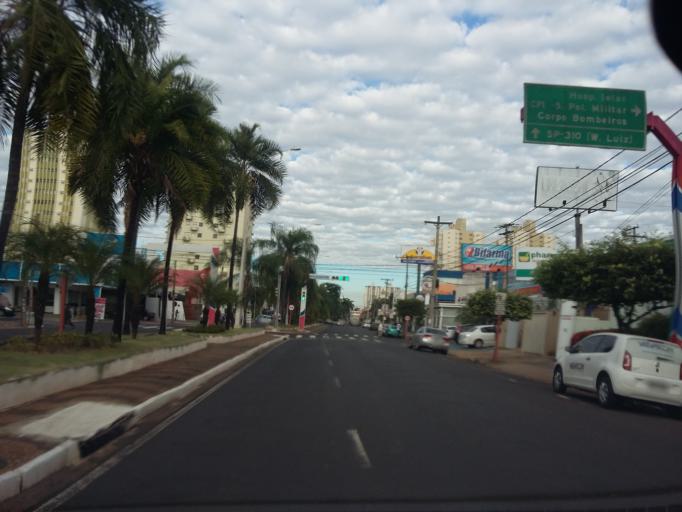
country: BR
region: Sao Paulo
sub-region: Sao Jose Do Rio Preto
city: Sao Jose do Rio Preto
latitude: -20.8134
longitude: -49.3900
